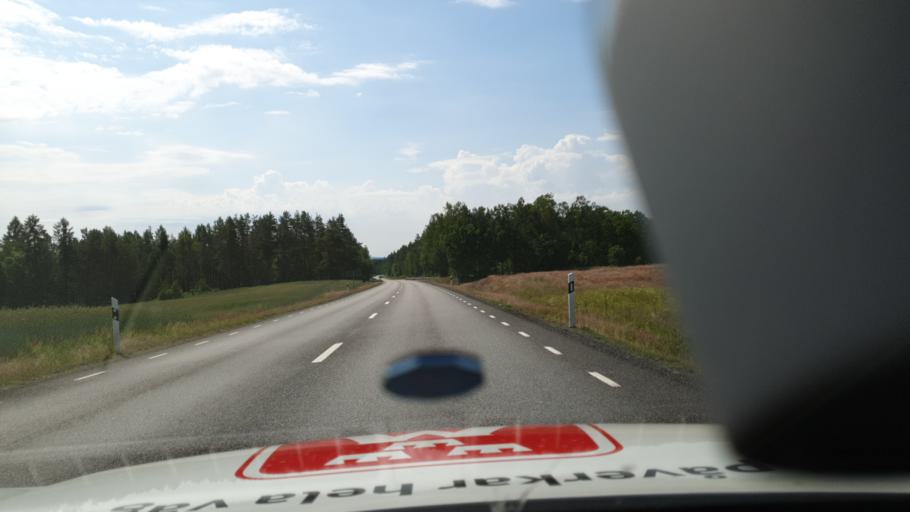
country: SE
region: Joenkoeping
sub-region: Habo Kommun
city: Habo
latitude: 57.9689
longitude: 14.1051
